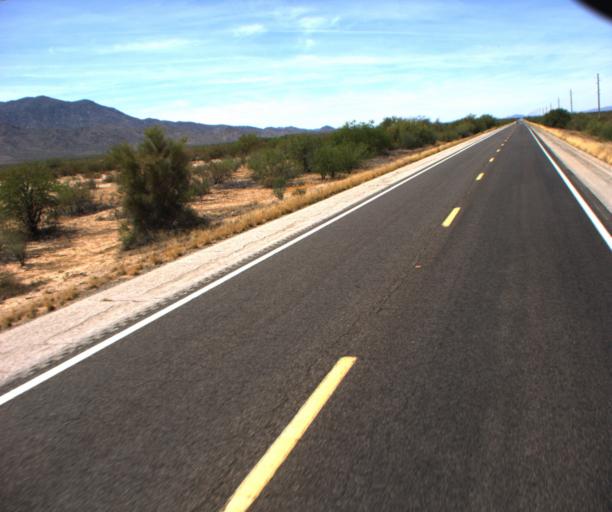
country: US
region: Arizona
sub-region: La Paz County
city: Salome
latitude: 33.9008
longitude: -113.3050
